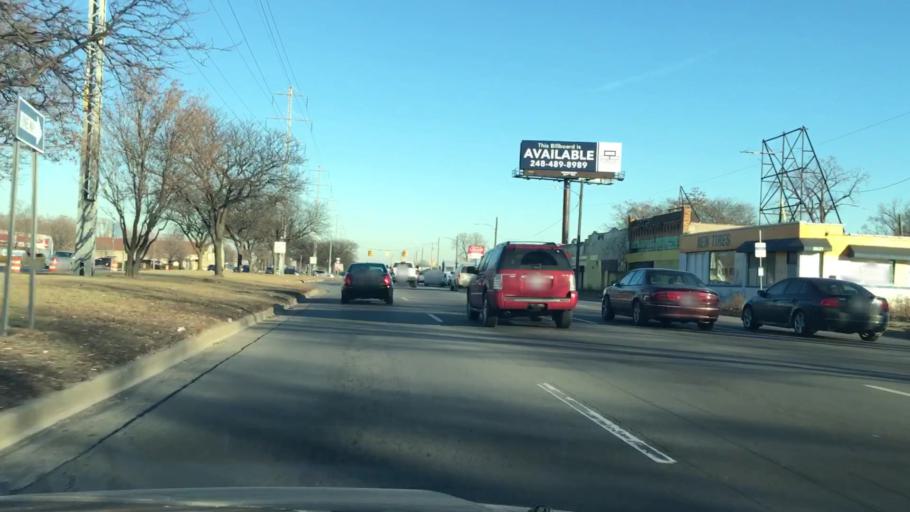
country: US
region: Michigan
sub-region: Oakland County
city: Ferndale
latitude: 42.4458
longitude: -83.1583
